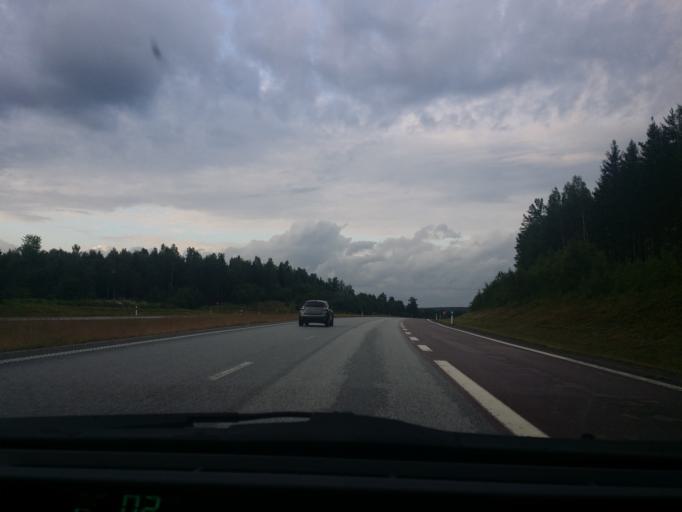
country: SE
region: Vaestmanland
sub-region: Kopings Kommun
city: Koping
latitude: 59.5123
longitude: 15.9458
